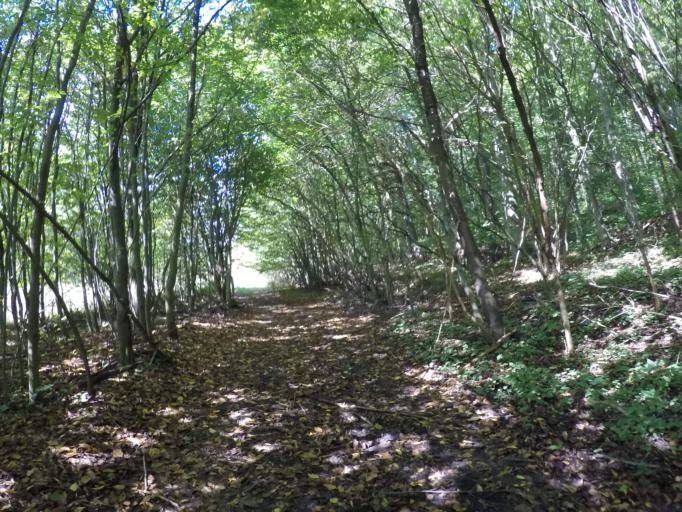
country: SK
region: Presovsky
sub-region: Okres Presov
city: Presov
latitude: 48.9350
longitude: 21.1594
